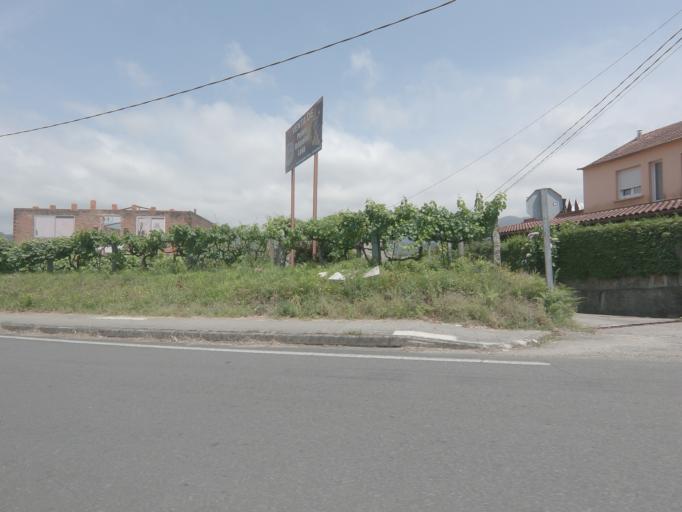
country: ES
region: Galicia
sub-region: Provincia de Pontevedra
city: Gondomar
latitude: 42.1038
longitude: -8.7596
